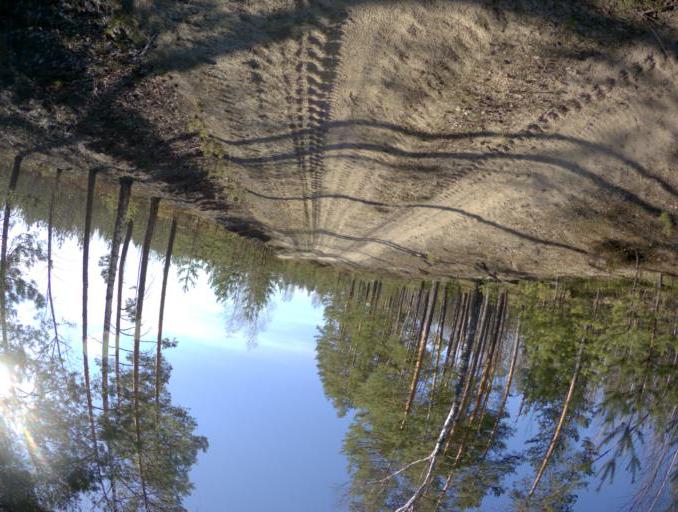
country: RU
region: Vladimir
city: Ivanishchi
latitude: 55.7023
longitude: 40.4383
